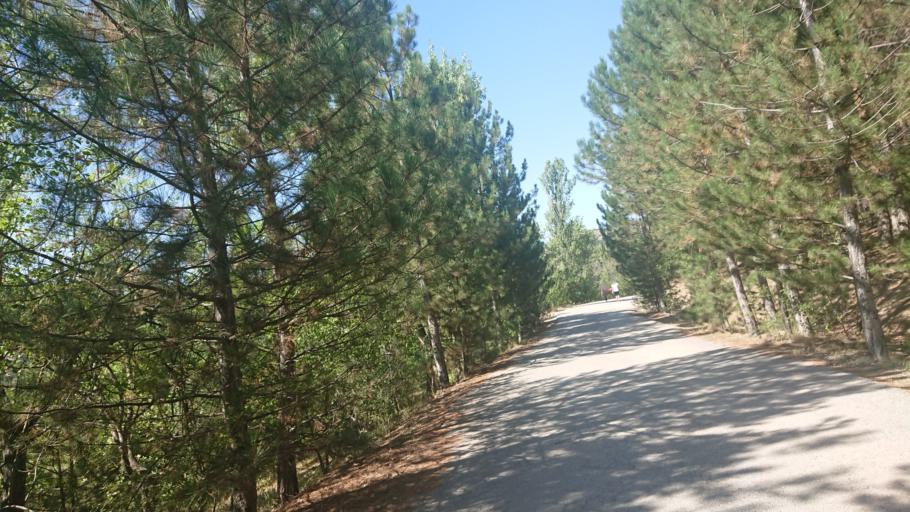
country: TR
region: Ankara
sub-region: Goelbasi
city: Golbasi
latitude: 39.8169
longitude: 32.8211
